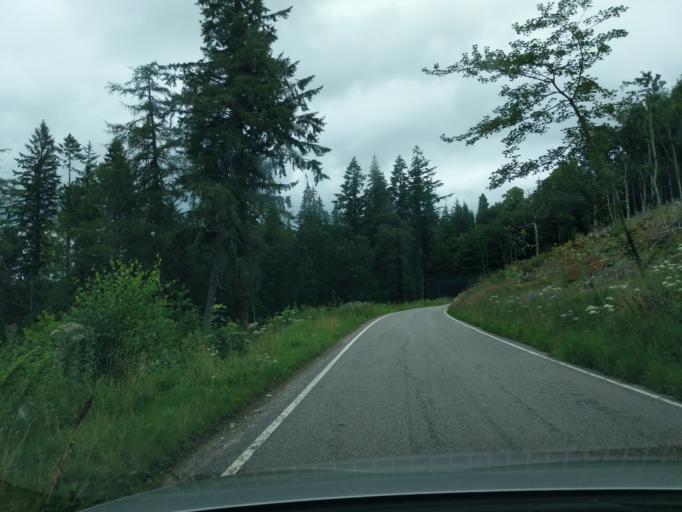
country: GB
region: Scotland
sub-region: Moray
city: Forres
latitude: 57.5228
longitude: -3.6727
